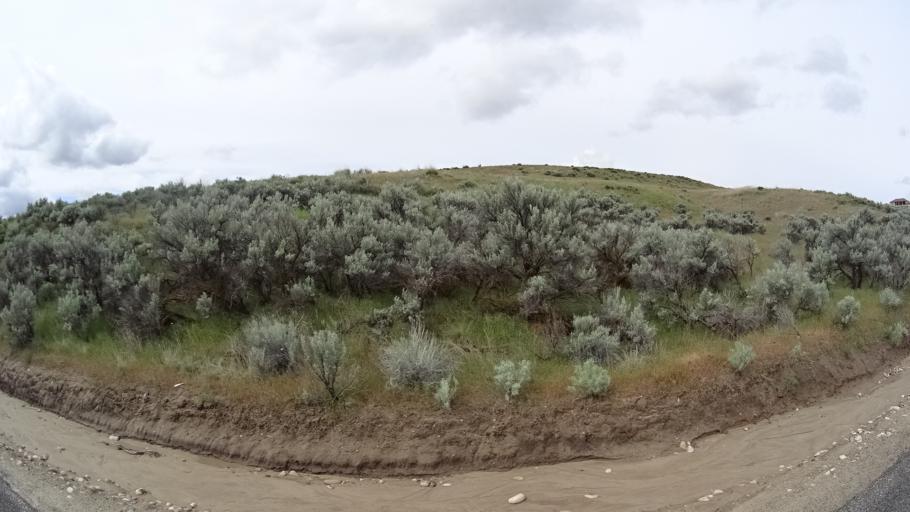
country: US
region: Idaho
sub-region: Ada County
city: Eagle
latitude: 43.7532
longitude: -116.3620
